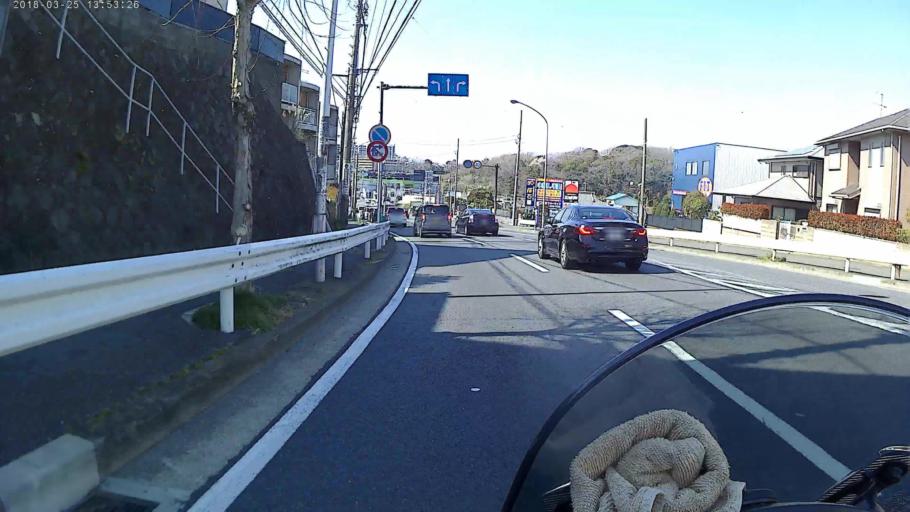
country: JP
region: Kanagawa
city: Fujisawa
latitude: 35.3818
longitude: 139.5024
